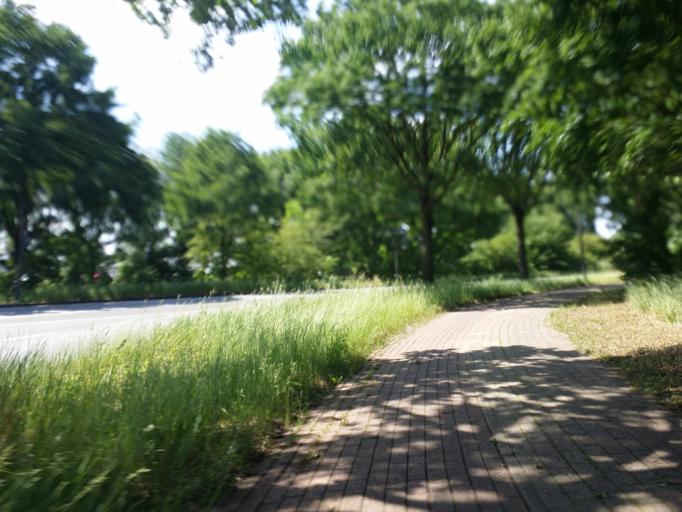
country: DE
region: Lower Saxony
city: Stuhr
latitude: 53.0813
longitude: 8.7540
